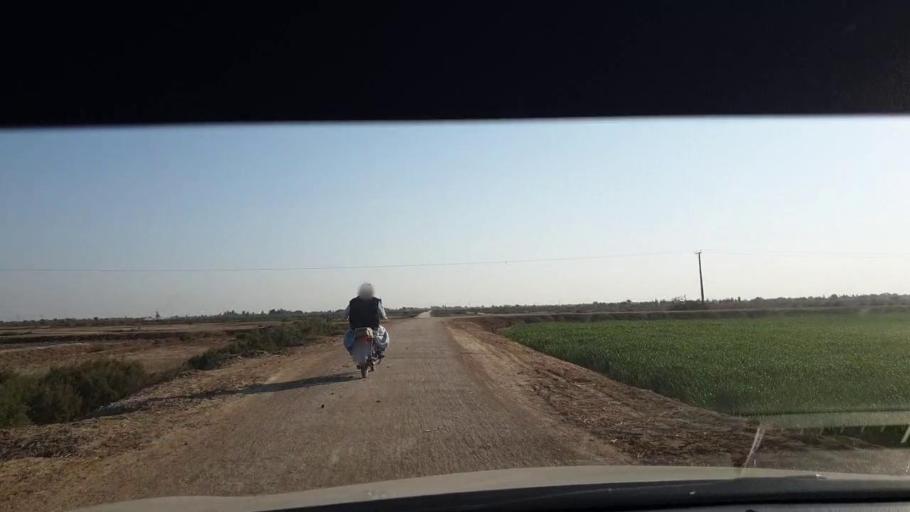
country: PK
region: Sindh
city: Berani
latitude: 25.7905
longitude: 68.9264
